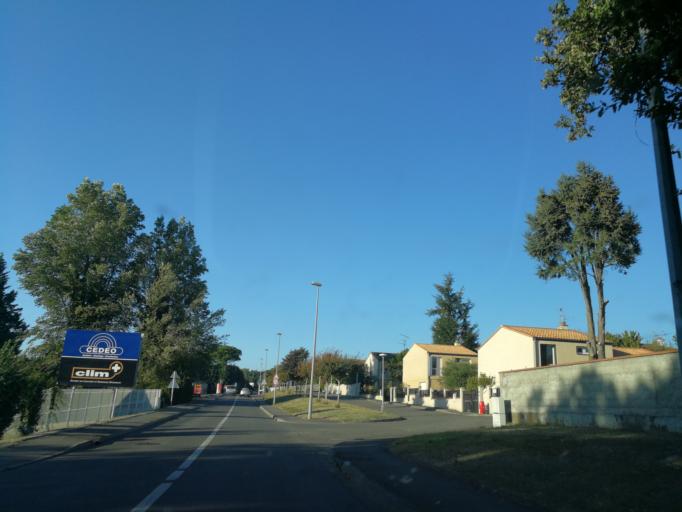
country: FR
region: Midi-Pyrenees
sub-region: Departement de la Haute-Garonne
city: L'Union
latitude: 43.6608
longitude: 1.4708
